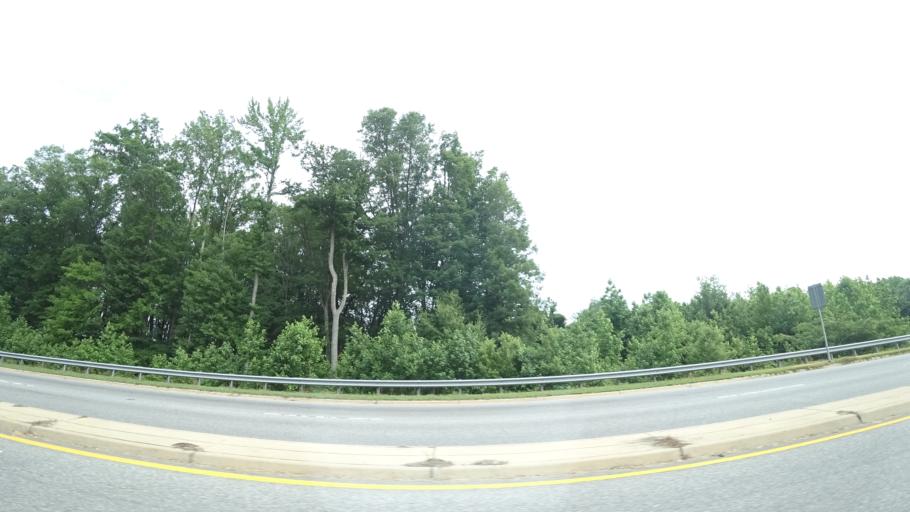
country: US
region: Virginia
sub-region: Spotsylvania County
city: Spotsylvania
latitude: 38.2060
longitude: -77.5989
